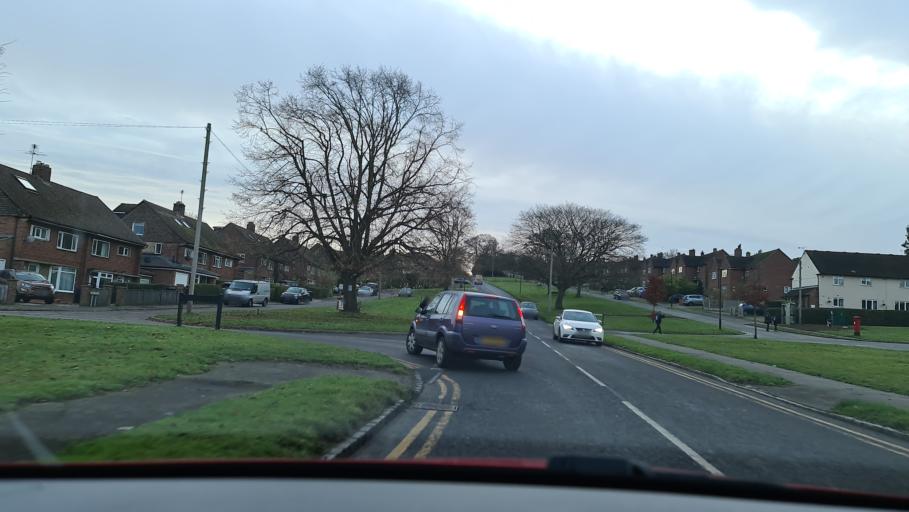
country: GB
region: England
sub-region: Buckinghamshire
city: Princes Risborough
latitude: 51.7228
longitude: -0.8281
